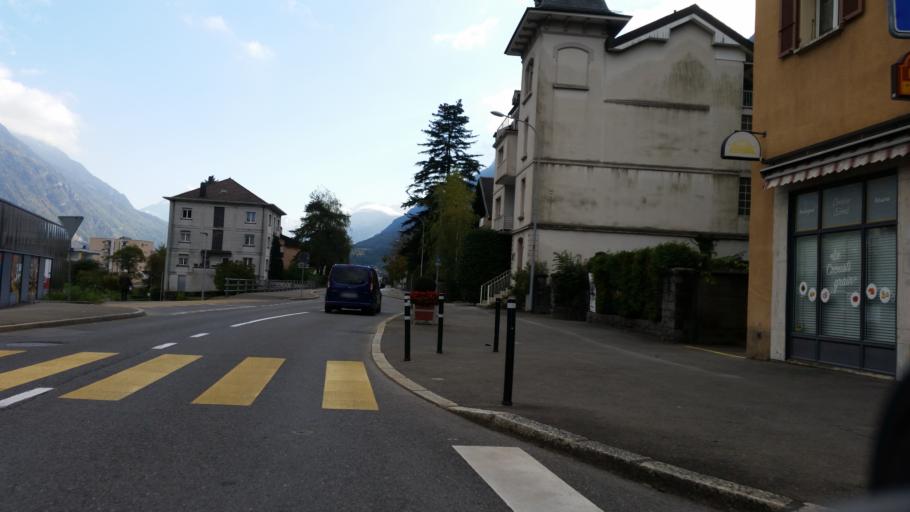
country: CH
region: Valais
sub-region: Saint-Maurice District
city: Saint-Maurice
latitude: 46.2149
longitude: 7.0048
